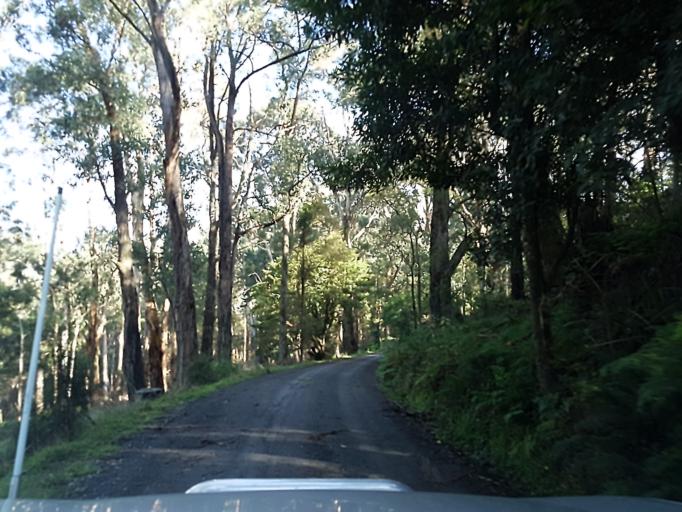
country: AU
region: Victoria
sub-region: Yarra Ranges
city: Belgrave
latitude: -37.9058
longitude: 145.3628
